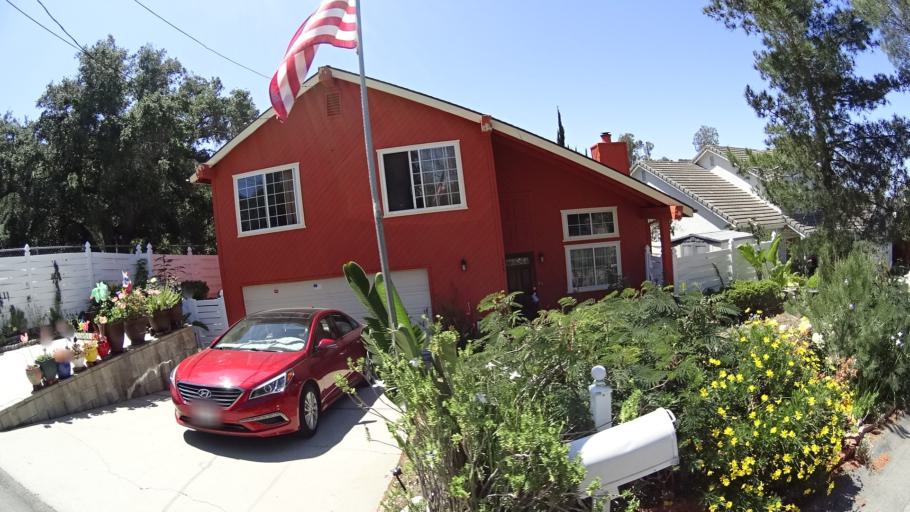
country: US
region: California
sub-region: Ventura County
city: Casa Conejo
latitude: 34.1719
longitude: -118.9077
